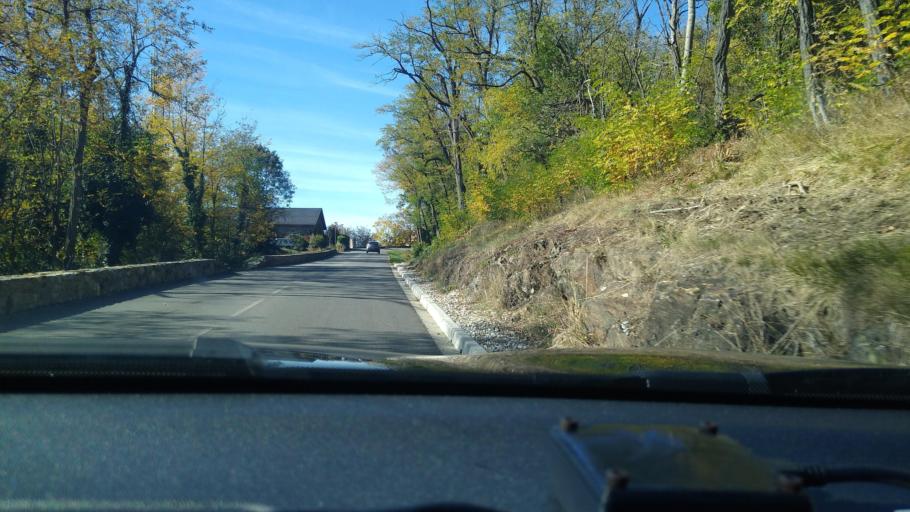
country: FR
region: Midi-Pyrenees
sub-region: Departement de l'Ariege
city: Ax-les-Thermes
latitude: 42.7234
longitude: 1.8420
